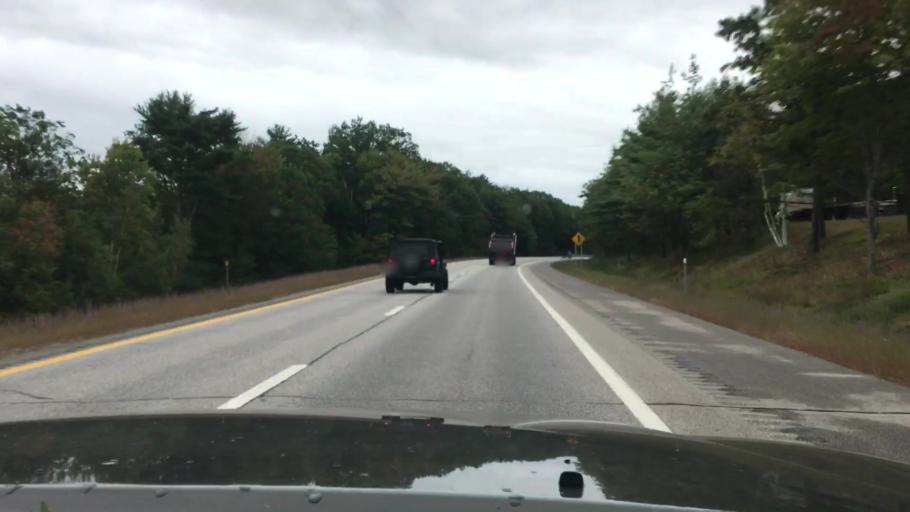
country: US
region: New Hampshire
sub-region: Belknap County
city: Sanbornton
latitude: 43.4924
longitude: -71.5992
